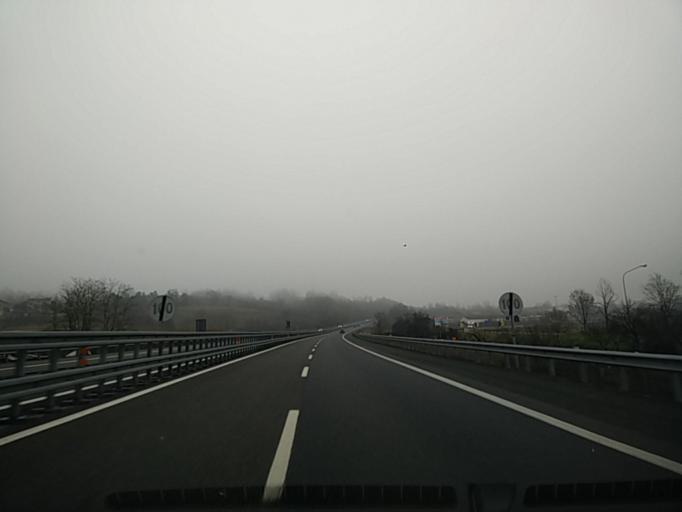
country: IT
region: Piedmont
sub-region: Provincia di Asti
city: Baldichieri d'Asti
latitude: 44.9045
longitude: 8.0965
